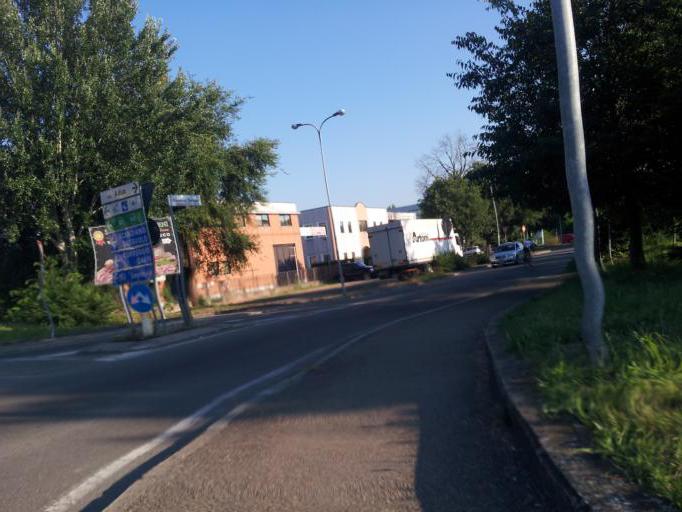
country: IT
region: Emilia-Romagna
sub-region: Provincia di Reggio Emilia
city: Reggio nell'Emilia
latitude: 44.7050
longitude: 10.6568
